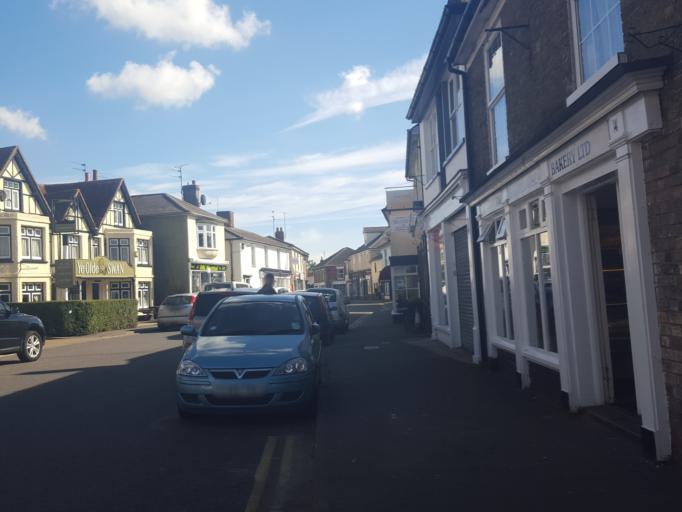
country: GB
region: England
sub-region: Essex
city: Brightlingsea
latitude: 51.8107
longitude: 1.0263
